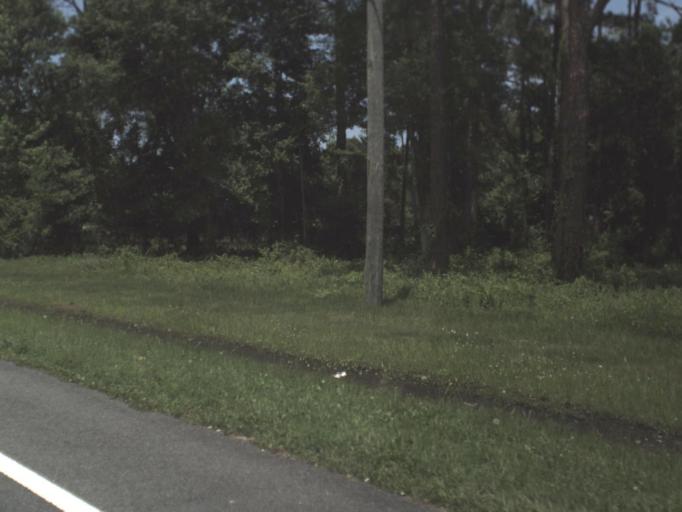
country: US
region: Florida
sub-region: Nassau County
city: Yulee
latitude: 30.5063
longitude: -81.6229
